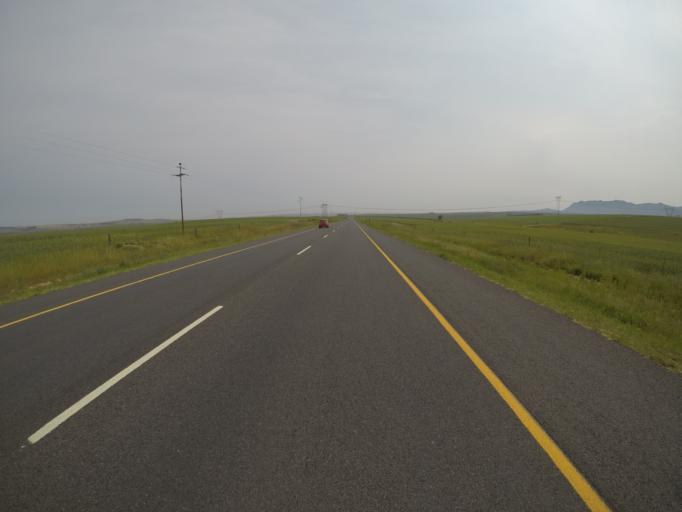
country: ZA
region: Western Cape
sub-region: West Coast District Municipality
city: Malmesbury
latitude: -33.4965
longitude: 18.8300
